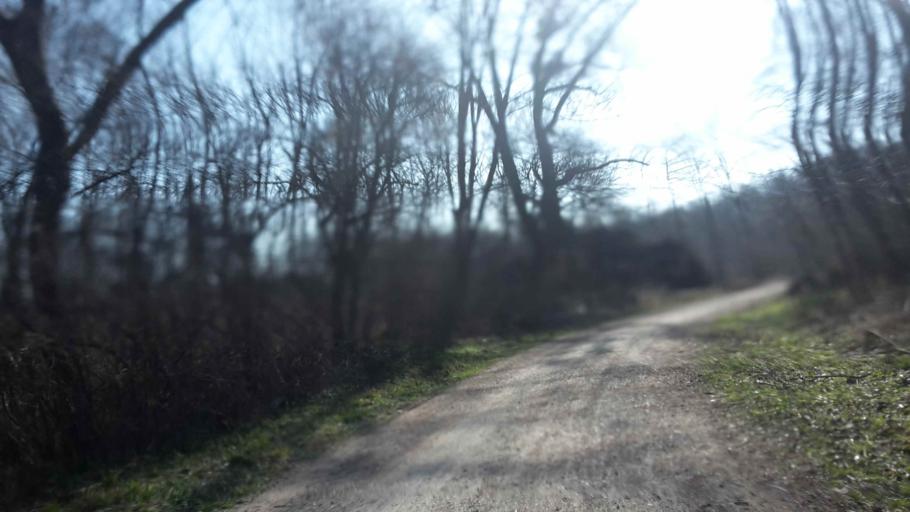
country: DE
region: Bavaria
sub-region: Upper Bavaria
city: Unterfoehring
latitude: 48.2076
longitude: 11.6416
